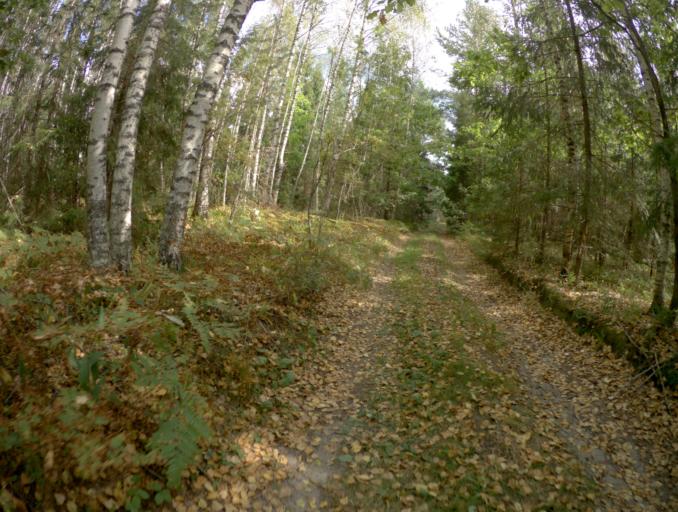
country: RU
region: Vladimir
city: Orgtrud
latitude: 56.1124
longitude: 40.6953
